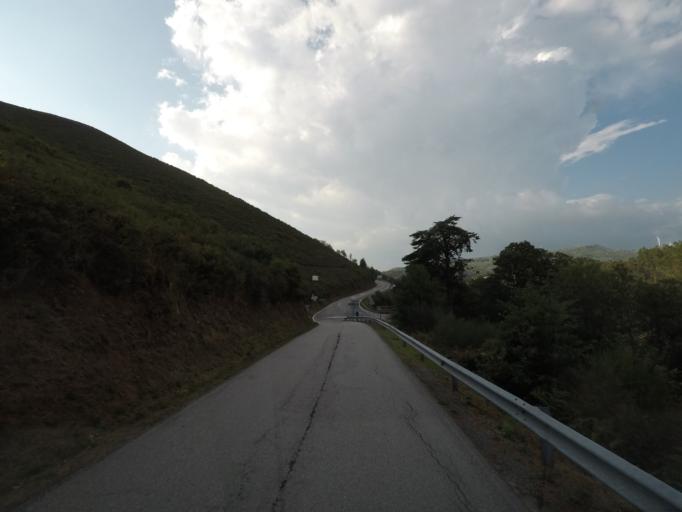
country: PT
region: Porto
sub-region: Baiao
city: Valadares
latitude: 41.1820
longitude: -7.9369
